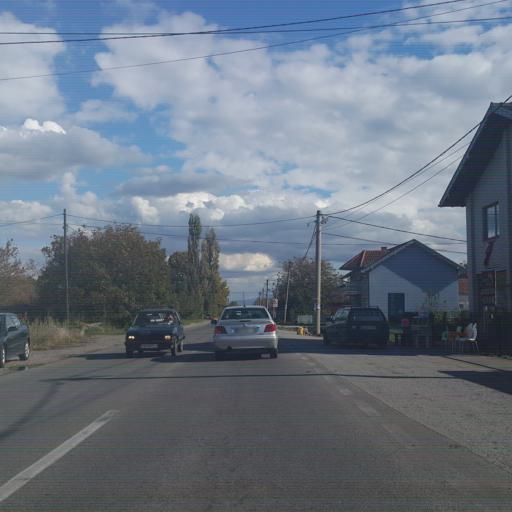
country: RS
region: Central Serbia
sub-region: Rasinski Okrug
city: Trstenik
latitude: 43.6002
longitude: 21.0506
